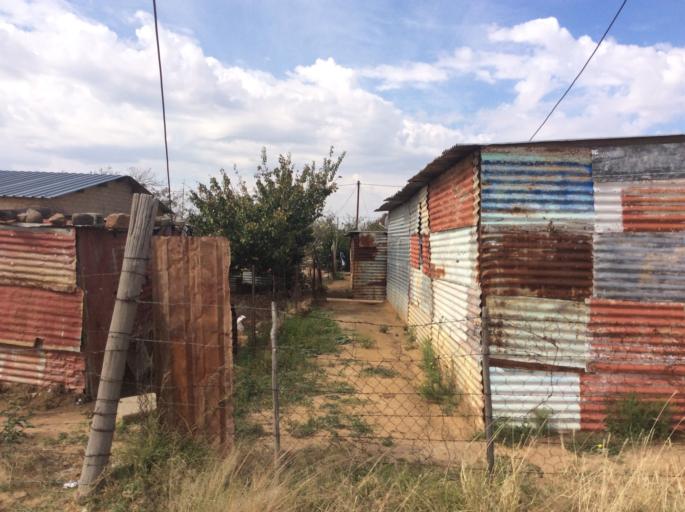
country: ZA
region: Orange Free State
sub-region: Xhariep District Municipality
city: Dewetsdorp
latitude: -29.5785
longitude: 26.6886
